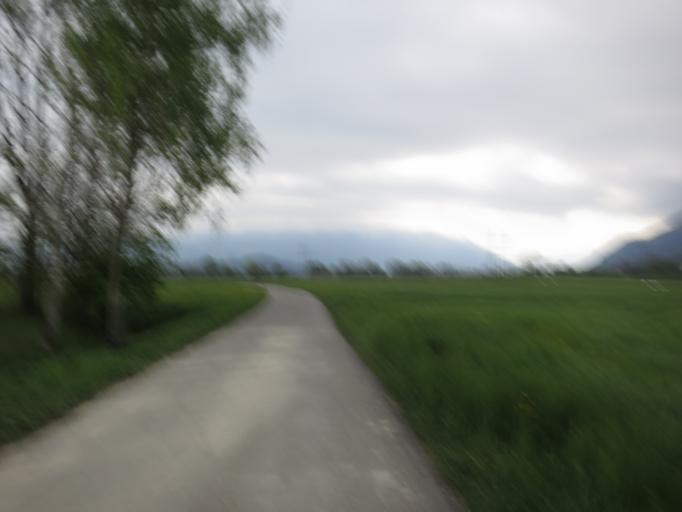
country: CH
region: Schwyz
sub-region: Bezirk March
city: Schubelbach
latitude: 47.1797
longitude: 8.9448
